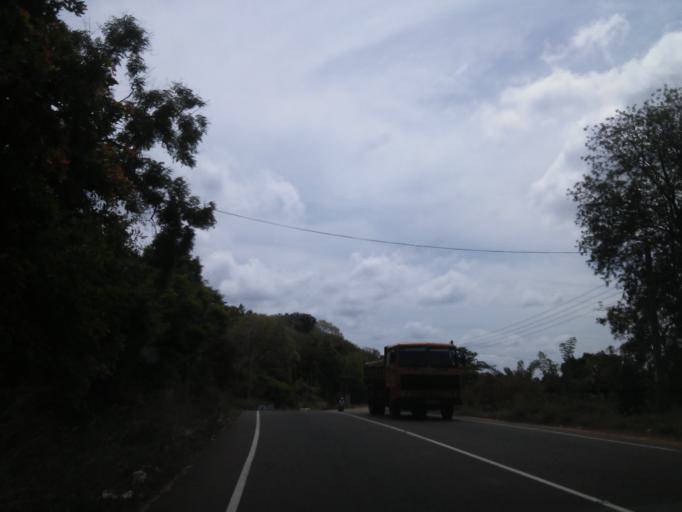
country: LK
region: Eastern Province
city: Trincomalee
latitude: 8.3428
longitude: 80.9815
